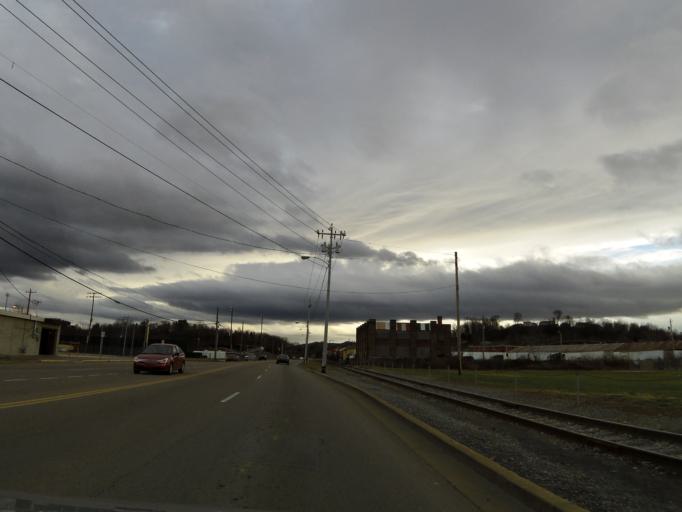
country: US
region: Tennessee
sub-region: Washington County
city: Johnson City
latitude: 36.3192
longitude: -82.3434
